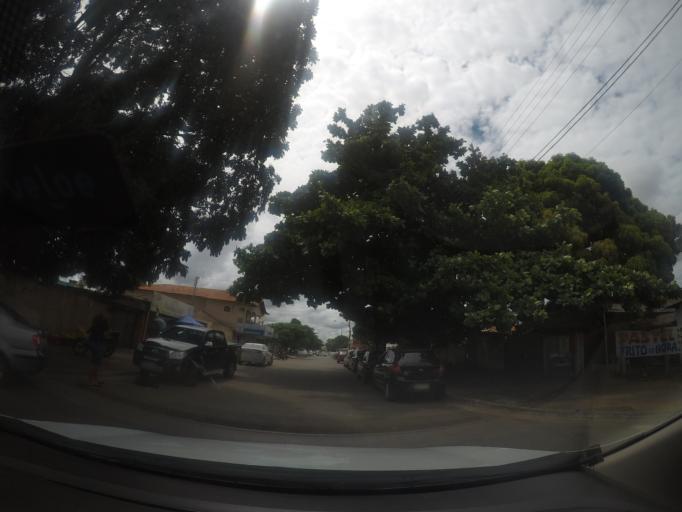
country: BR
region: Goias
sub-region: Goiania
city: Goiania
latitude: -16.6634
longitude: -49.3043
